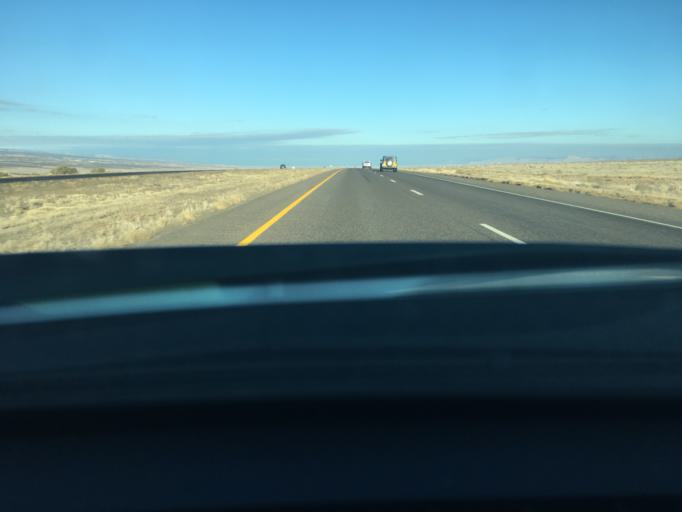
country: US
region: Colorado
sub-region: Delta County
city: Delta
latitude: 38.8461
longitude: -108.3020
